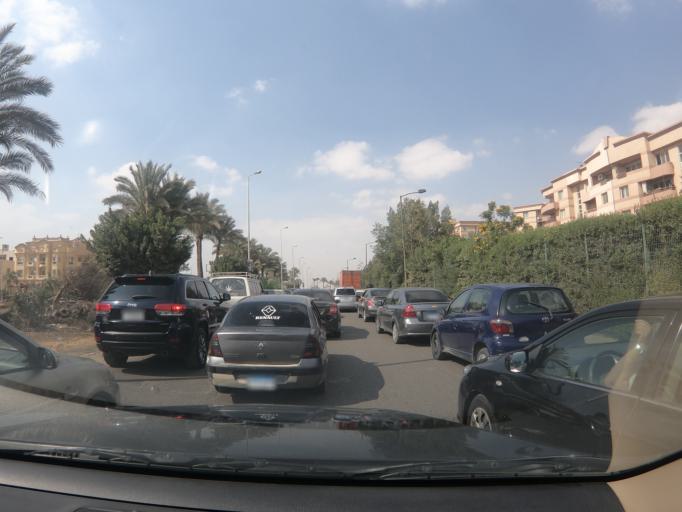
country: EG
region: Muhafazat al Qalyubiyah
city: Al Khankah
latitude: 30.0681
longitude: 31.4750
